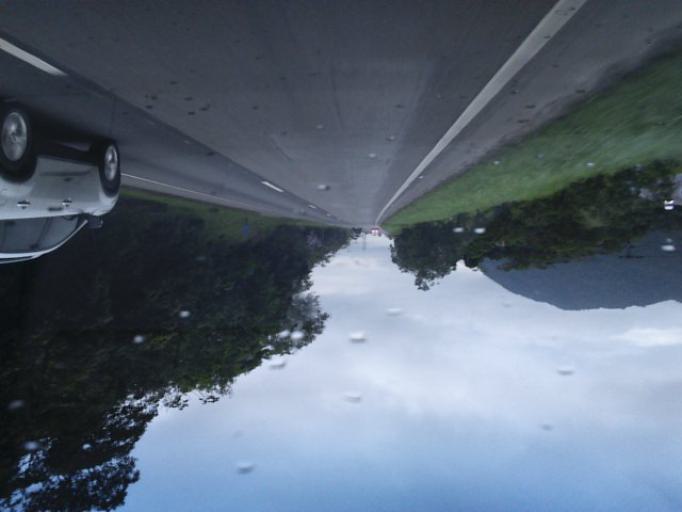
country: BR
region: Parana
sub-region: Guaratuba
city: Guaratuba
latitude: -25.9237
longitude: -48.9157
